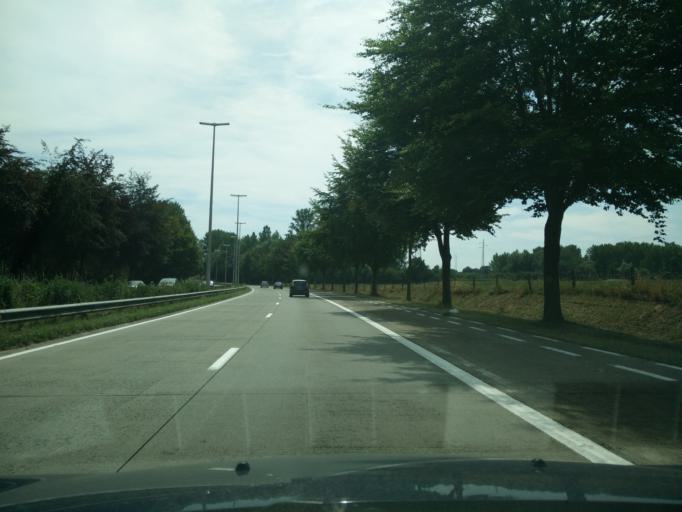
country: BE
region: Flanders
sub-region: Provincie Oost-Vlaanderen
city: Ninove
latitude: 50.8616
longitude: 4.0244
